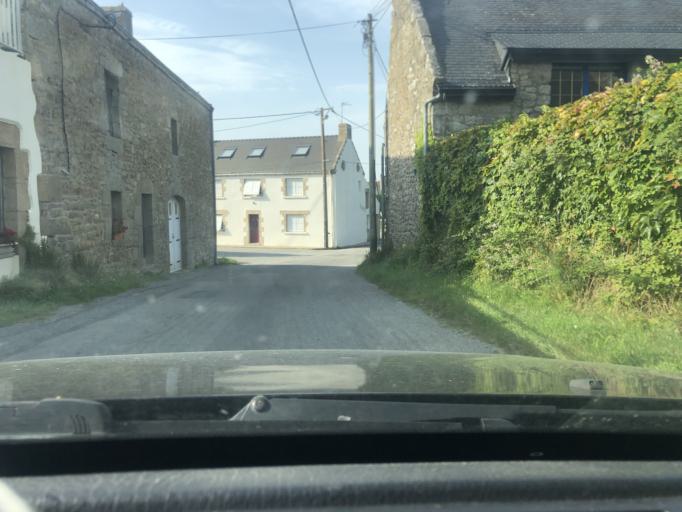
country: FR
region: Brittany
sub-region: Departement du Morbihan
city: Erdeven
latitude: 47.6264
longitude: -3.1806
